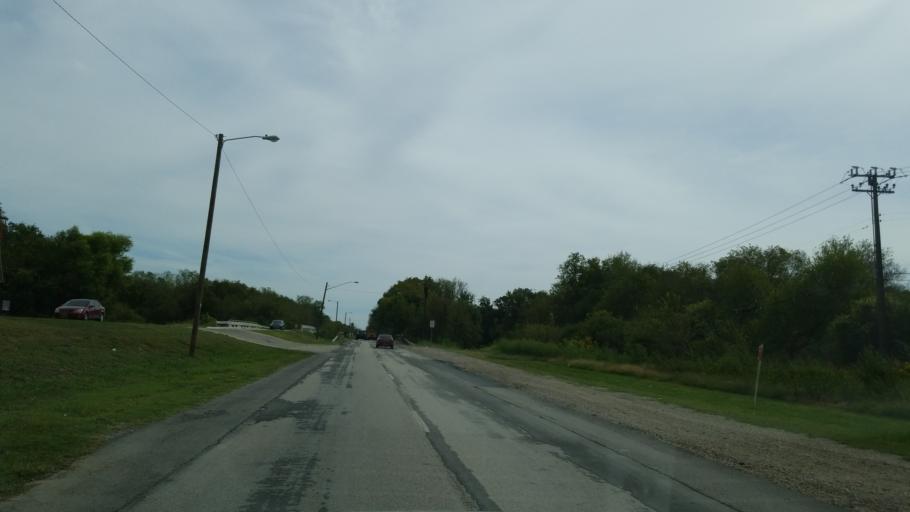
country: US
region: Texas
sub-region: Dallas County
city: Dallas
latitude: 32.7563
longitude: -96.7391
